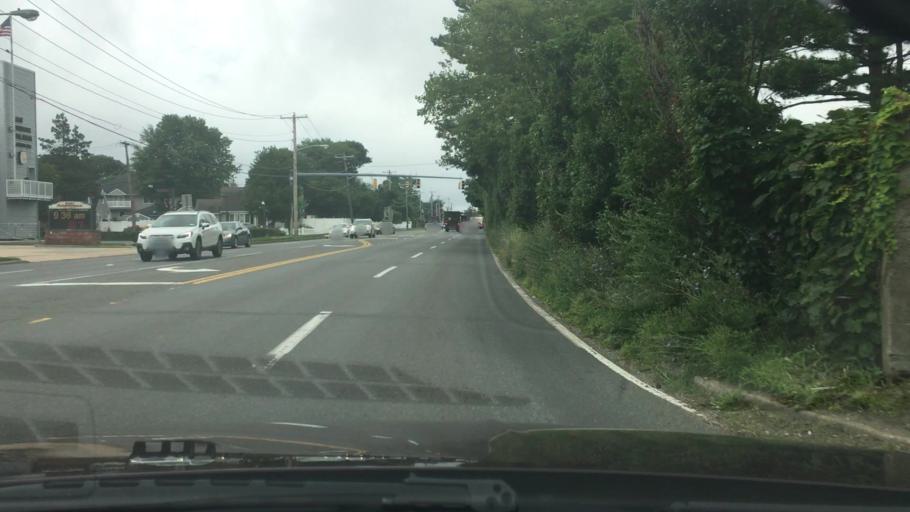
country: US
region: New York
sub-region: Suffolk County
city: North Lindenhurst
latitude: 40.7194
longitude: -73.3938
